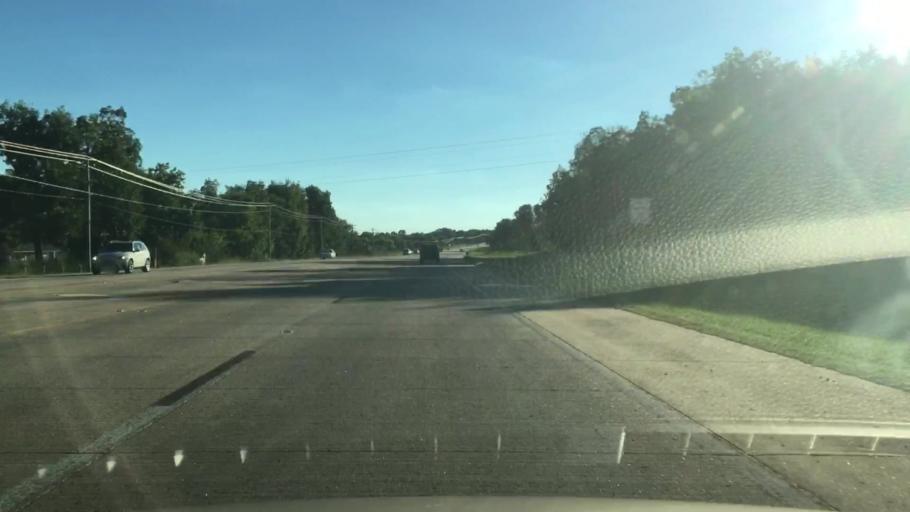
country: US
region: Oklahoma
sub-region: Cherokee County
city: Park Hill
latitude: 35.8276
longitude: -95.0464
